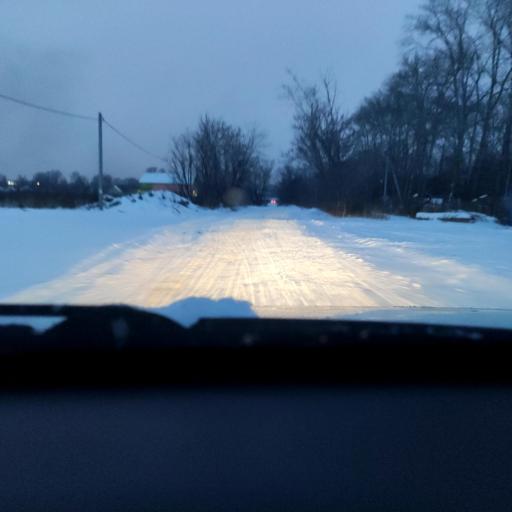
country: RU
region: Perm
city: Froly
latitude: 57.9482
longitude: 56.2310
